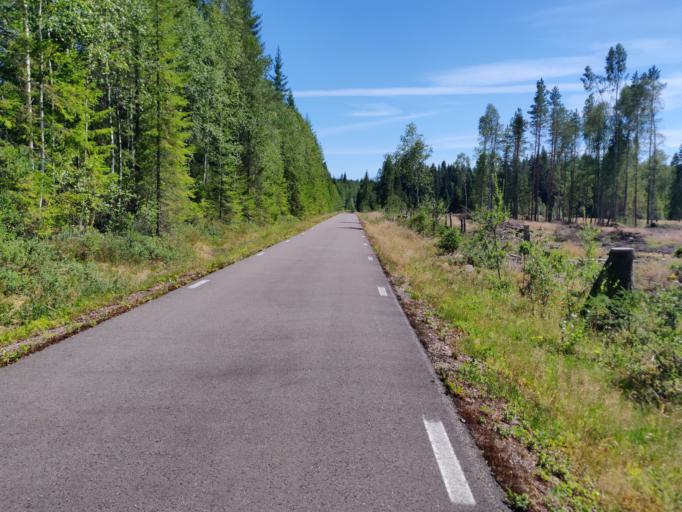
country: SE
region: Vaermland
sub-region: Munkfors Kommun
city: Munkfors
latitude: 59.9425
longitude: 13.5865
